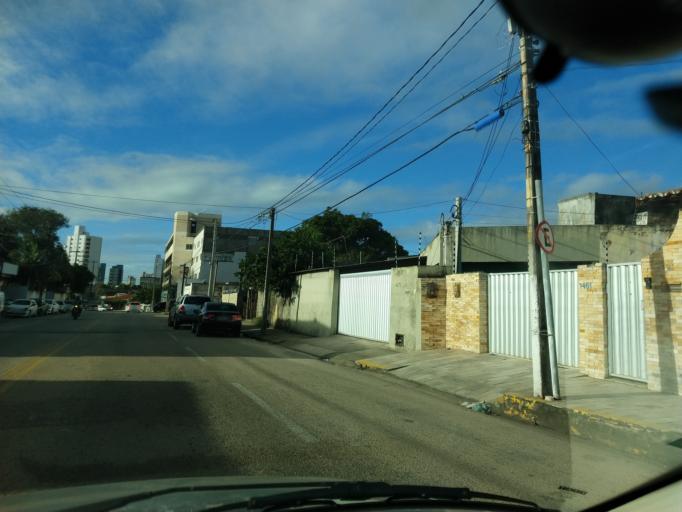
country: BR
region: Rio Grande do Norte
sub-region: Natal
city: Natal
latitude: -5.8023
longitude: -35.2123
